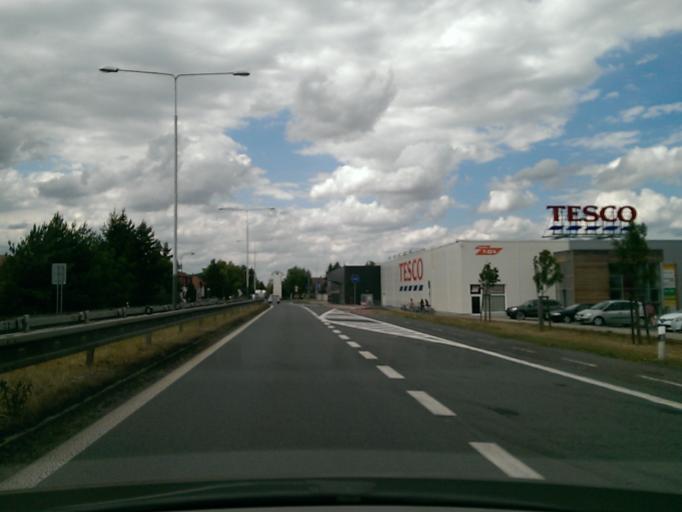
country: CZ
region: Central Bohemia
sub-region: Okres Nymburk
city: Podebrady
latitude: 50.1341
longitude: 15.0978
